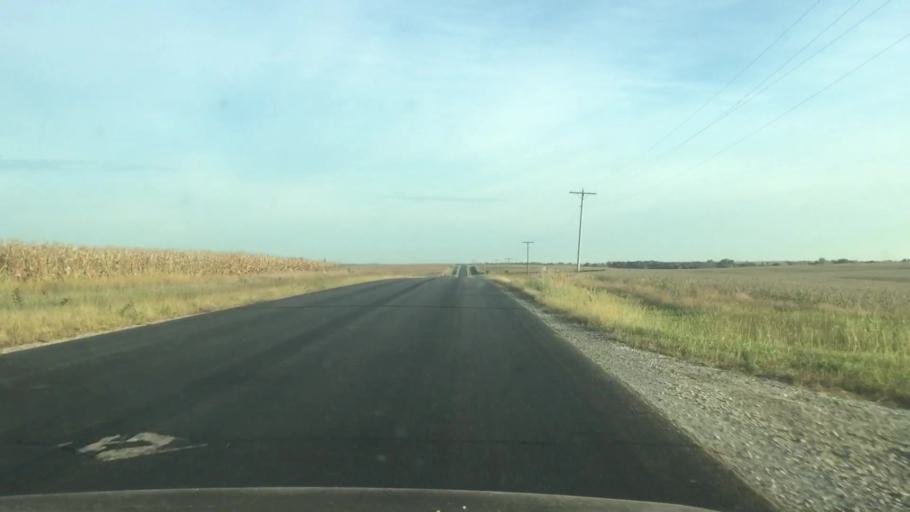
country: US
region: Kansas
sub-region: Marshall County
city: Marysville
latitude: 39.9072
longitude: -96.6010
